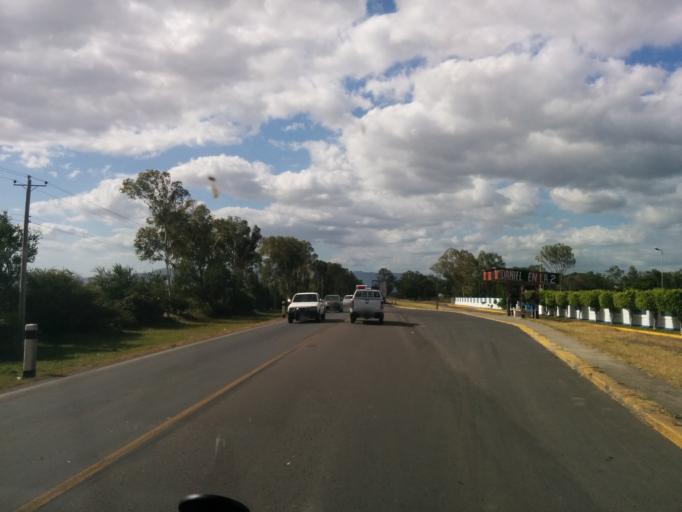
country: NI
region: Matagalpa
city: Ciudad Dario
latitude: 12.8626
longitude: -86.1106
